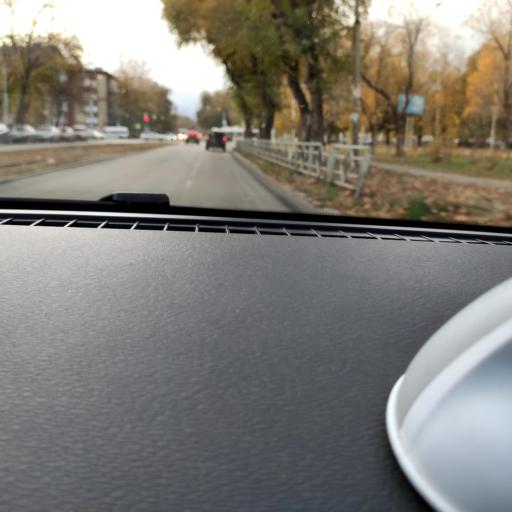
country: RU
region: Samara
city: Petra-Dubrava
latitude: 53.2395
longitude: 50.2818
